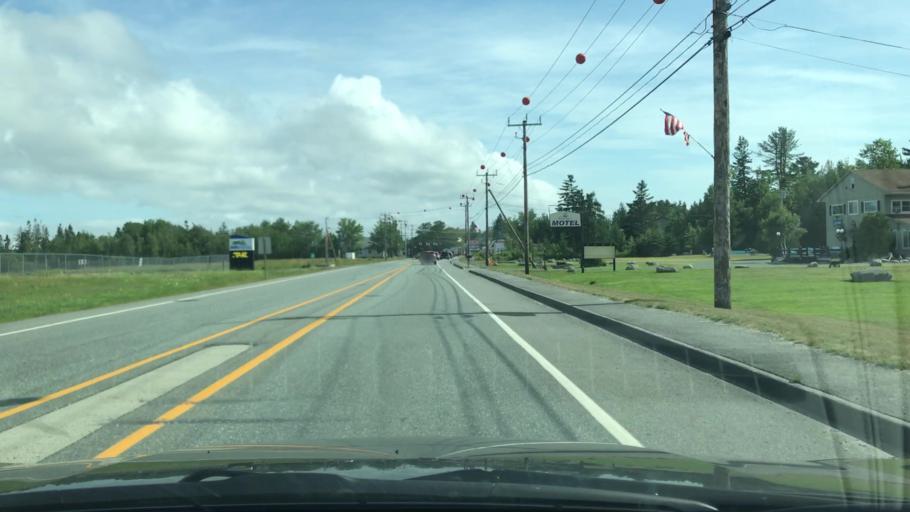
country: US
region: Maine
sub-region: Hancock County
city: Trenton
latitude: 44.4427
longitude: -68.3700
